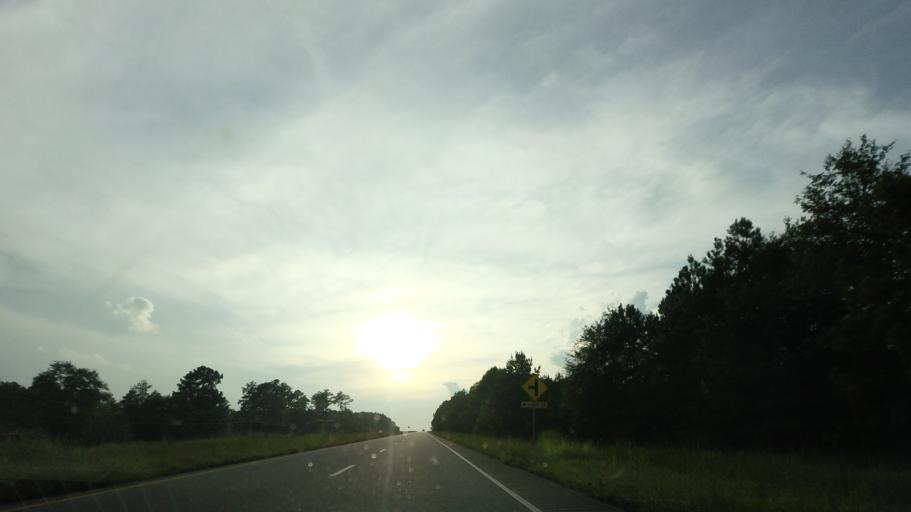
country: US
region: Georgia
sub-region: Wilkinson County
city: Gordon
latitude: 32.8484
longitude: -83.4296
